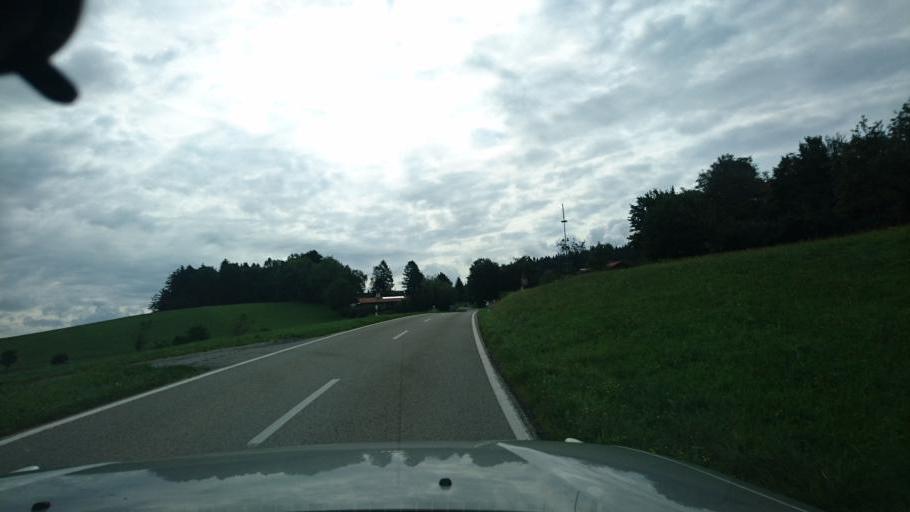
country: DE
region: Bavaria
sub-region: Upper Bavaria
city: Grabenstatt
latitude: 47.8349
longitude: 12.5608
